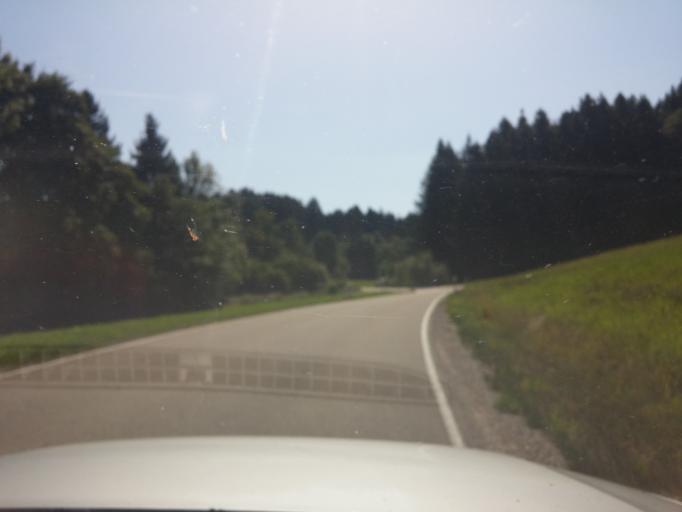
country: DE
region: Bavaria
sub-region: Swabia
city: Lautrach
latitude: 47.8757
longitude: 10.1052
